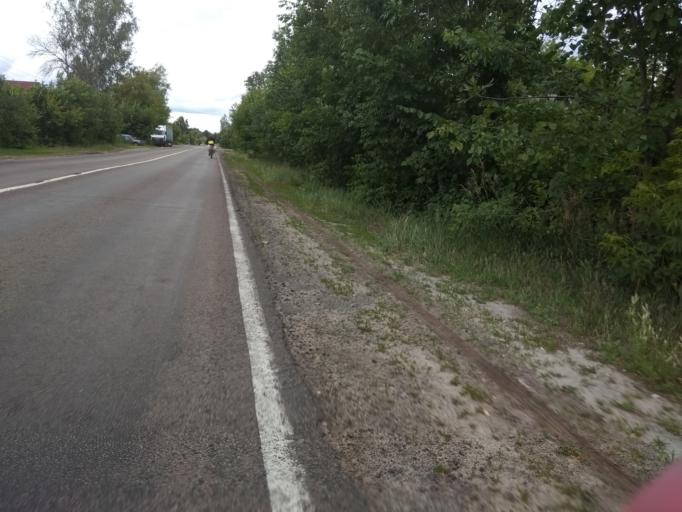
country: RU
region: Moskovskaya
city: Misheronskiy
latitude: 55.5973
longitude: 39.7038
